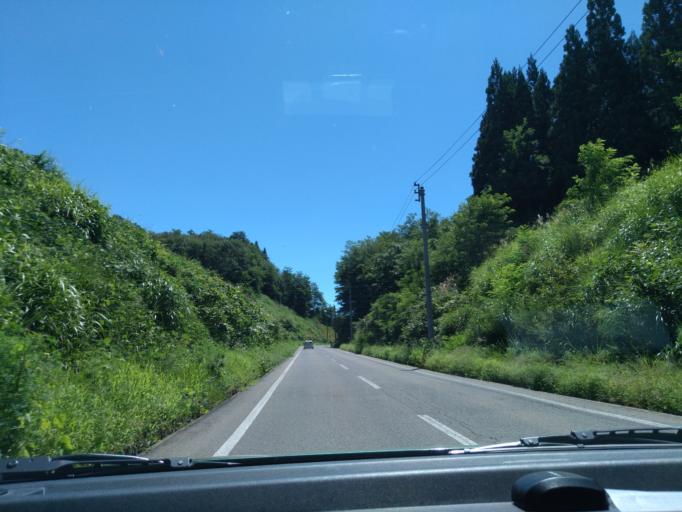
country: JP
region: Akita
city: Yokotemachi
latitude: 39.3787
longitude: 140.5826
